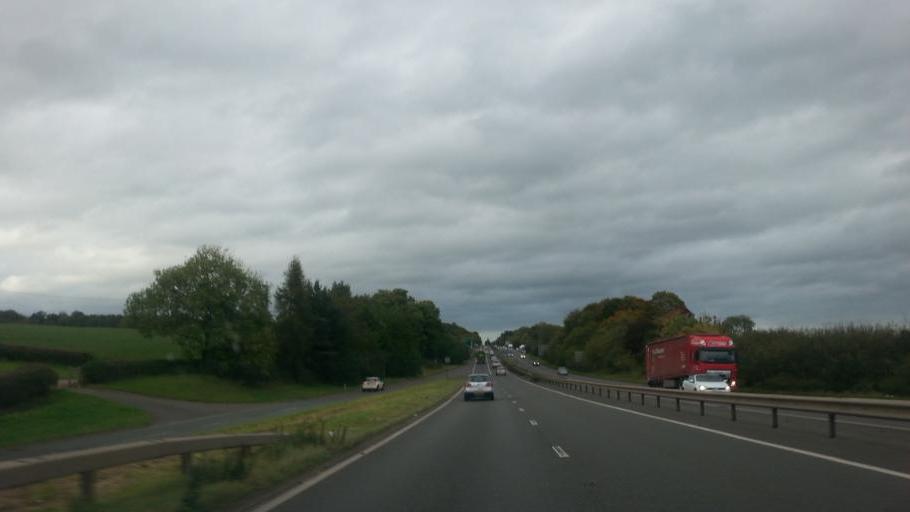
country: GB
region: England
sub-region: Leicestershire
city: Queniborough
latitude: 52.7166
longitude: -1.0779
